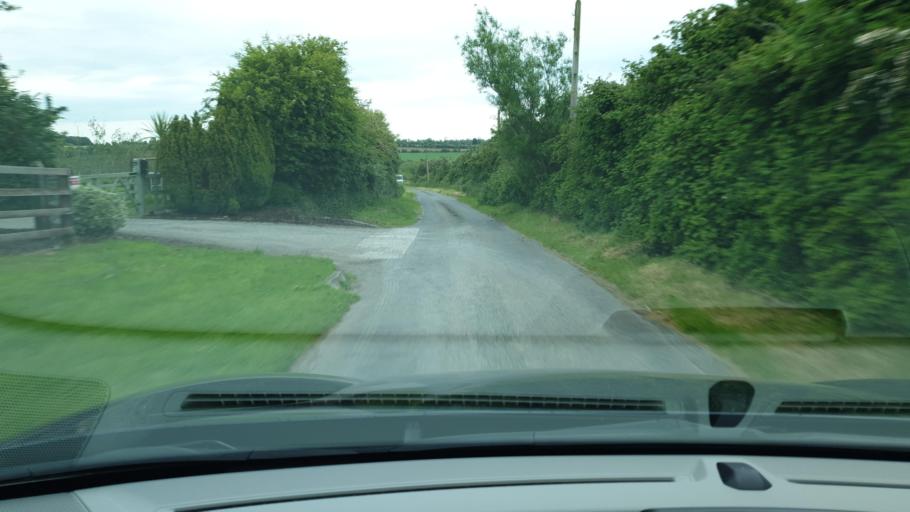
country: IE
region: Leinster
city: Balrothery
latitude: 53.5548
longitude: -6.2051
